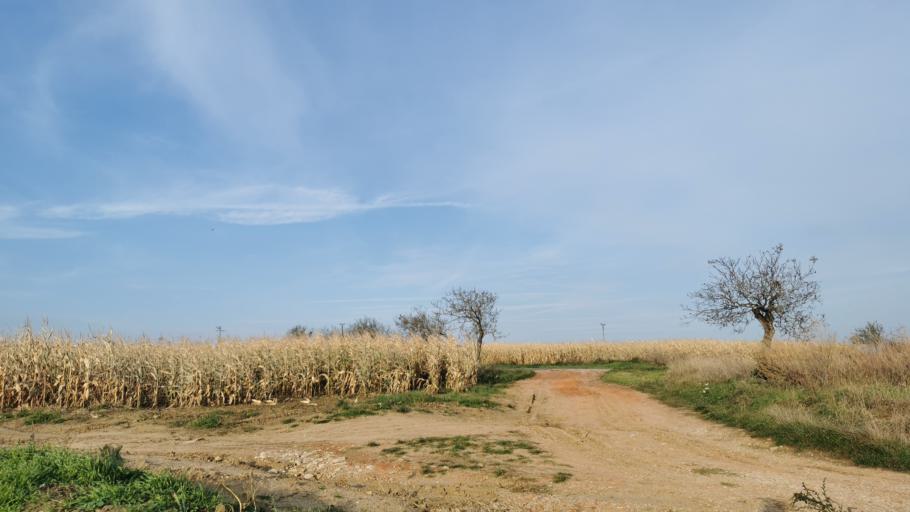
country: SK
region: Trnavsky
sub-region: Okres Skalica
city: Skalica
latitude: 48.8191
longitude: 17.2431
